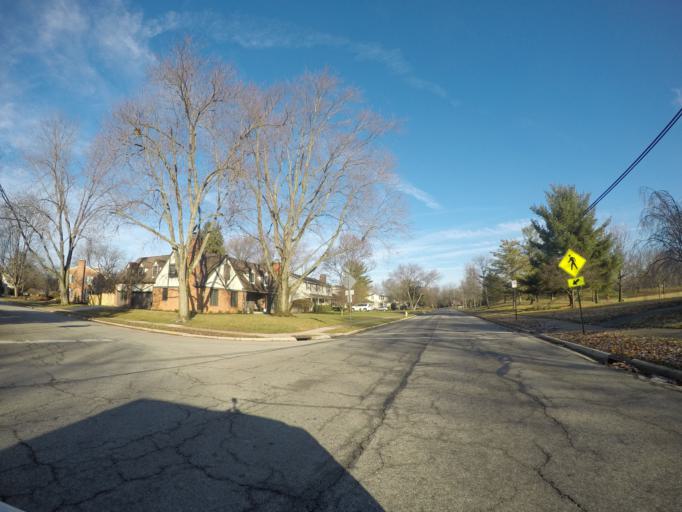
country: US
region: Ohio
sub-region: Franklin County
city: Upper Arlington
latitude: 40.0453
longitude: -83.0738
